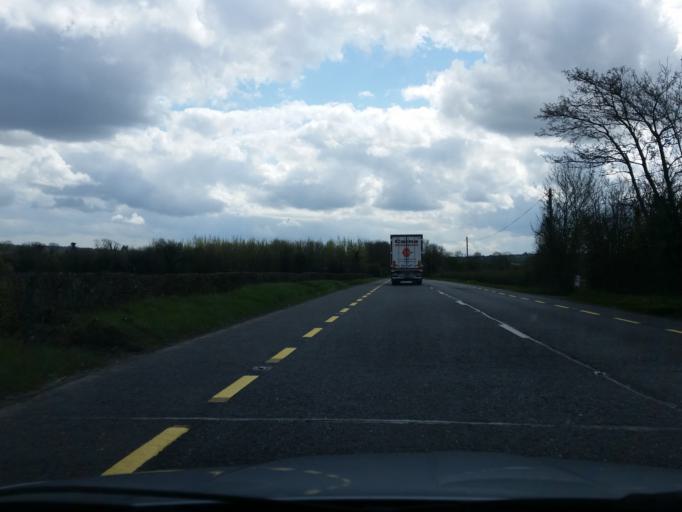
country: IE
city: Kentstown
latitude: 53.5933
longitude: -6.4651
